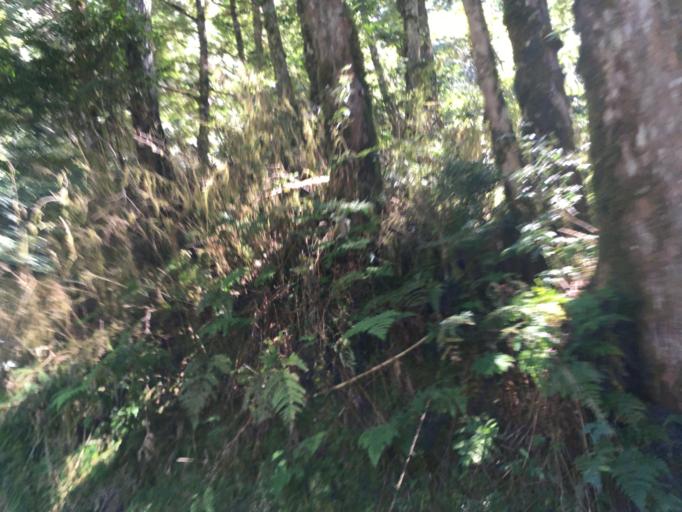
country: TW
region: Taiwan
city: Daxi
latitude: 24.5689
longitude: 121.4127
